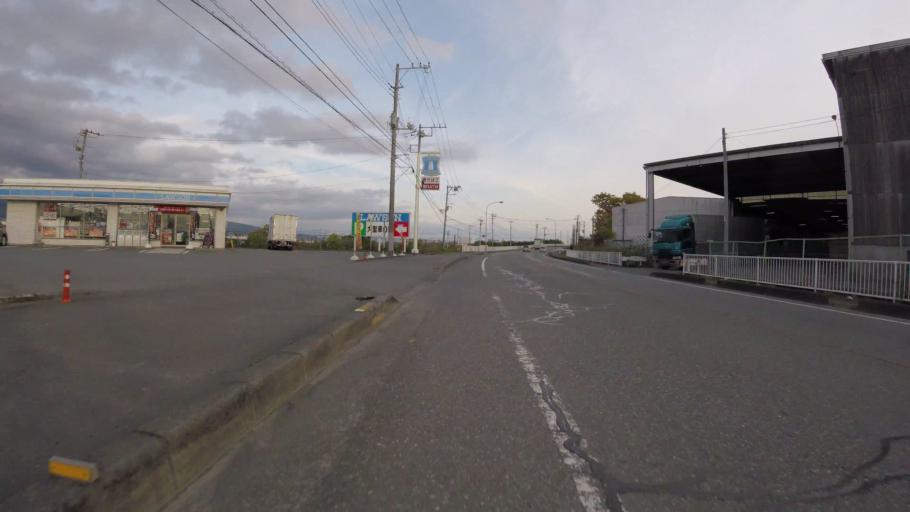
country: JP
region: Shizuoka
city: Fuji
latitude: 35.1467
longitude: 138.7161
